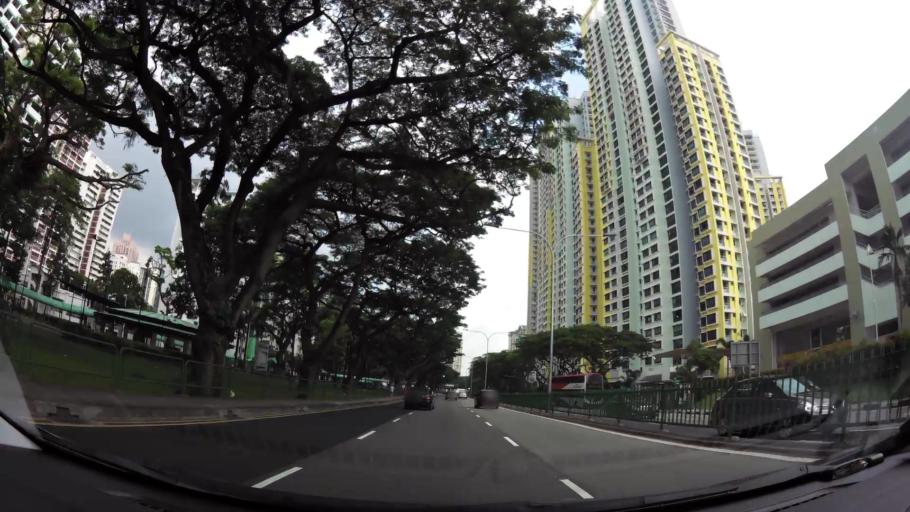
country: SG
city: Singapore
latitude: 1.2906
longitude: 103.8273
